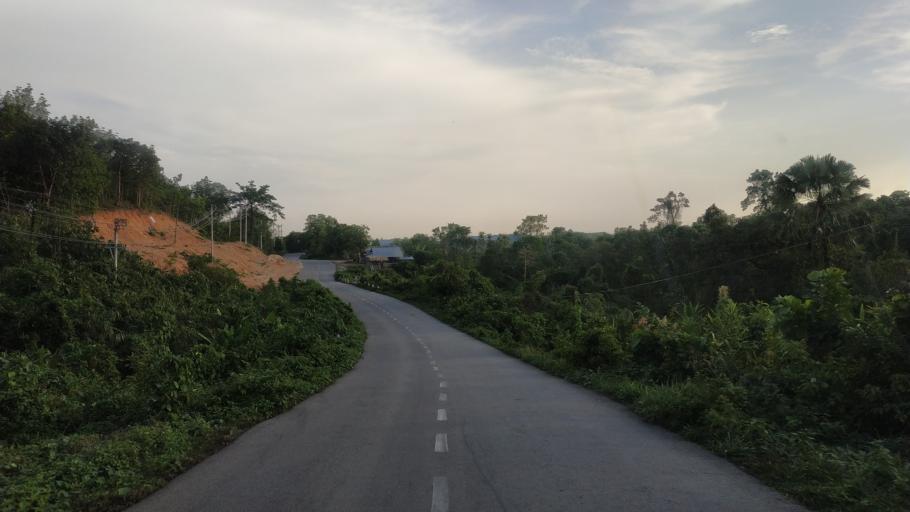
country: MM
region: Mon
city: Kyaikto
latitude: 17.4195
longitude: 97.0714
